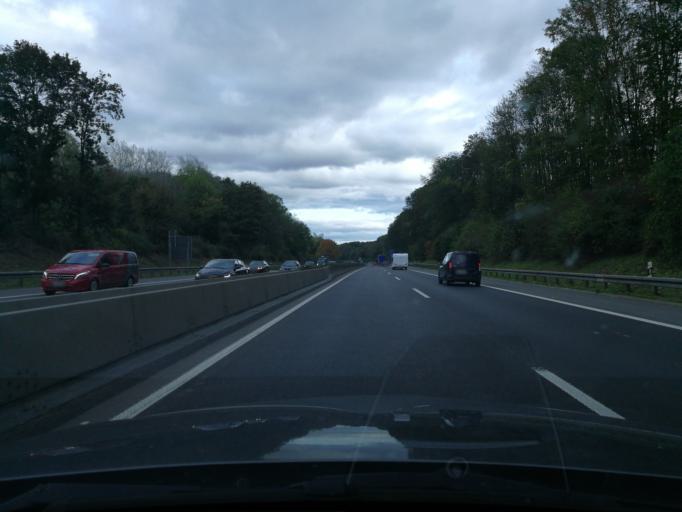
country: DE
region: North Rhine-Westphalia
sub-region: Regierungsbezirk Dusseldorf
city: Viersen
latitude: 51.2226
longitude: 6.4194
